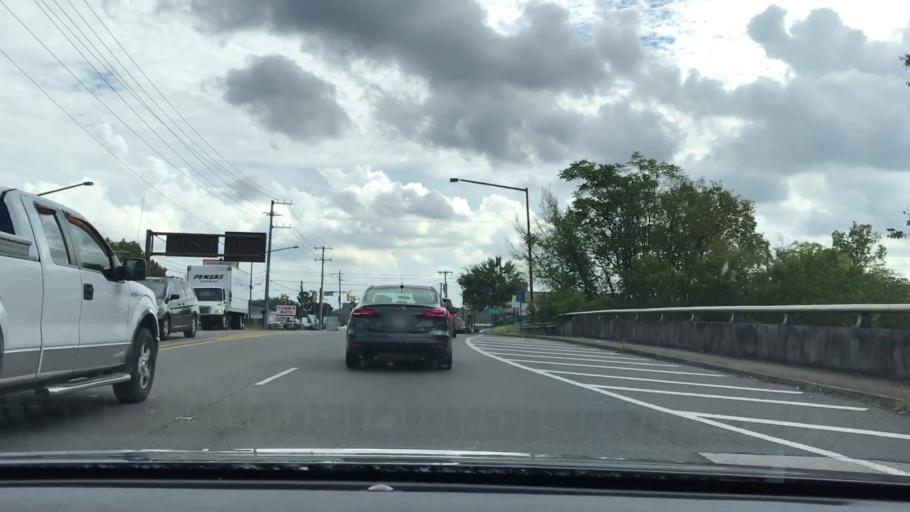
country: US
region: Tennessee
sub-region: Davidson County
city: Oak Hill
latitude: 36.1216
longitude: -86.7505
